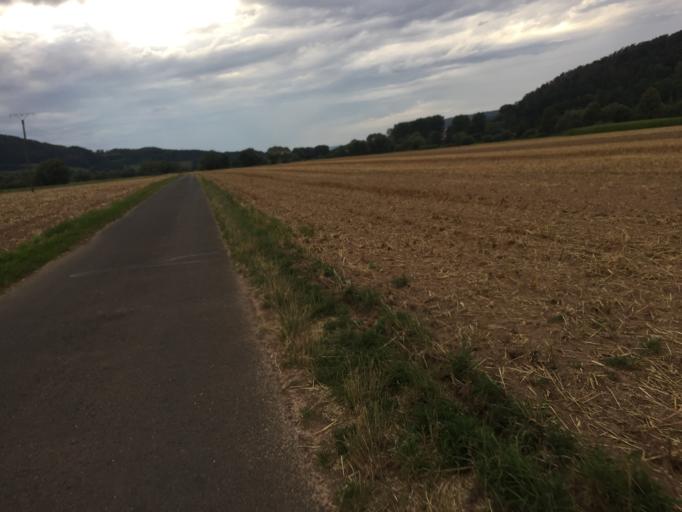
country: DE
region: Hesse
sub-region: Regierungsbezirk Kassel
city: Alheim
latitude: 51.0496
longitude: 9.6482
